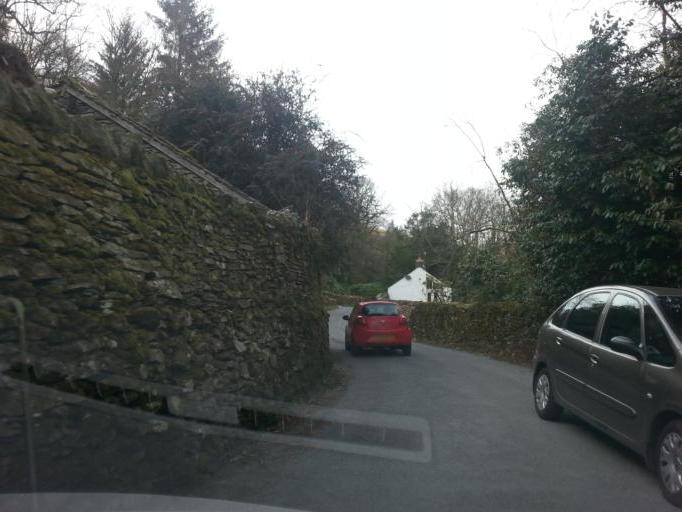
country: GB
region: England
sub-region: Cumbria
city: Ambleside
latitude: 54.4481
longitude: -3.0286
